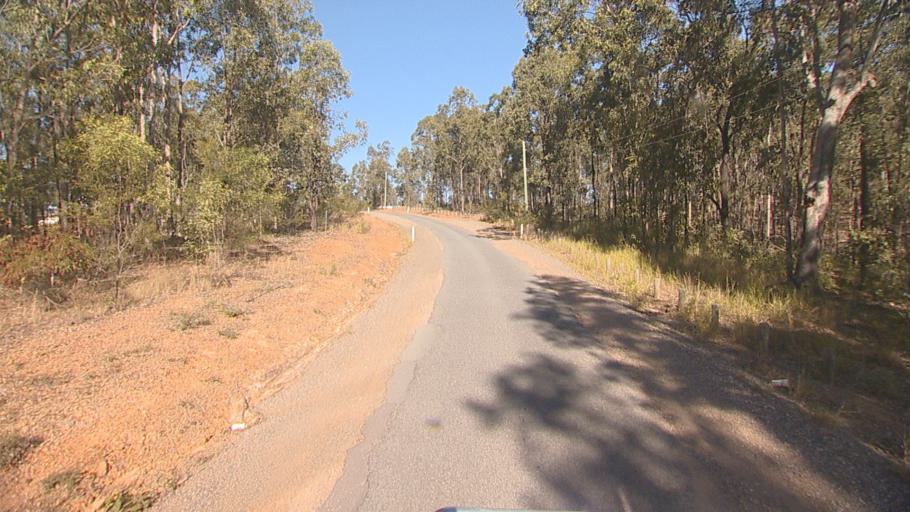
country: AU
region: Queensland
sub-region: Ipswich
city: Springfield Lakes
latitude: -27.7196
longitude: 152.9135
